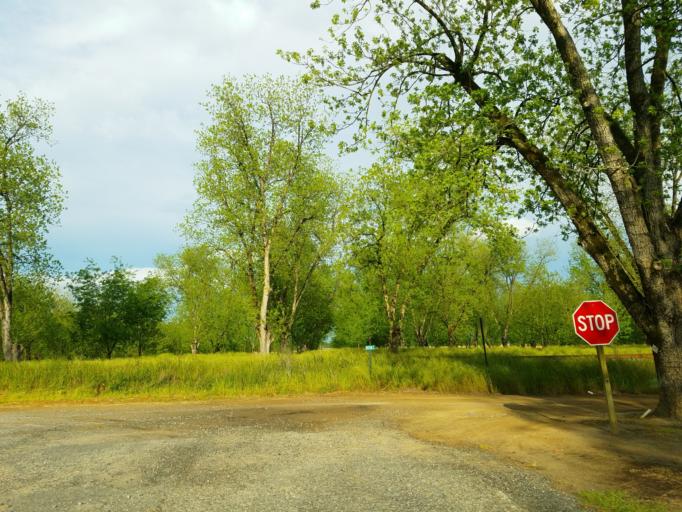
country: US
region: Georgia
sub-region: Dooly County
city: Vienna
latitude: 32.0420
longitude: -83.7866
